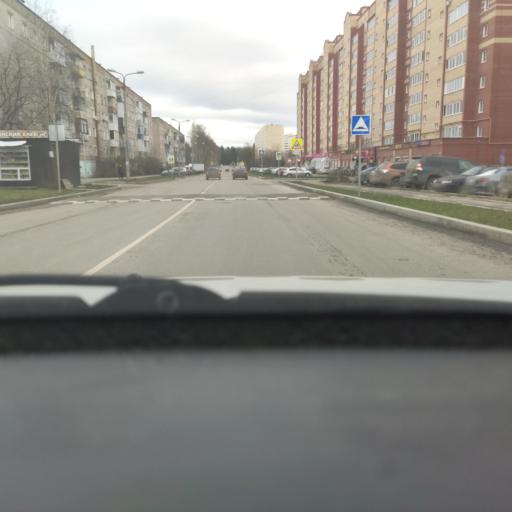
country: RU
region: Perm
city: Perm
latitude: 58.0846
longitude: 56.4033
